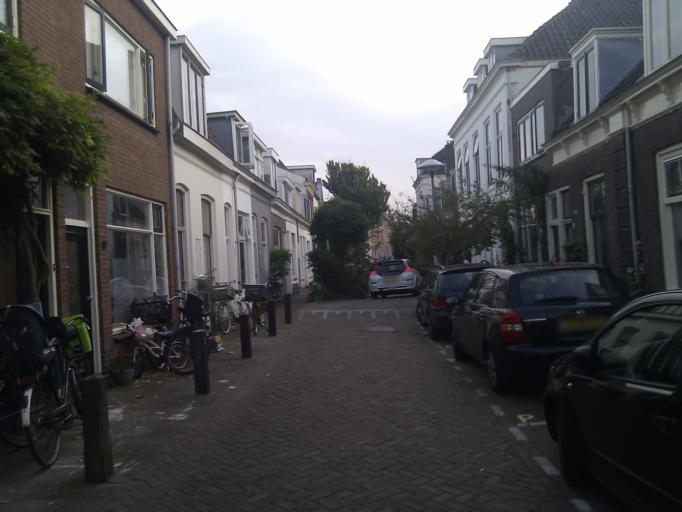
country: NL
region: Utrecht
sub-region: Gemeente Utrecht
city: Utrecht
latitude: 52.0979
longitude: 5.1293
